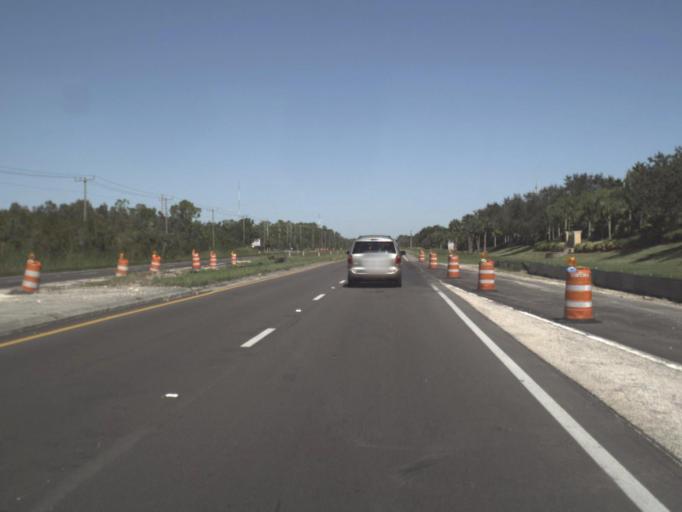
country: US
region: Florida
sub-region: Collier County
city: Lely Resort
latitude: 26.0329
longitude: -81.7005
